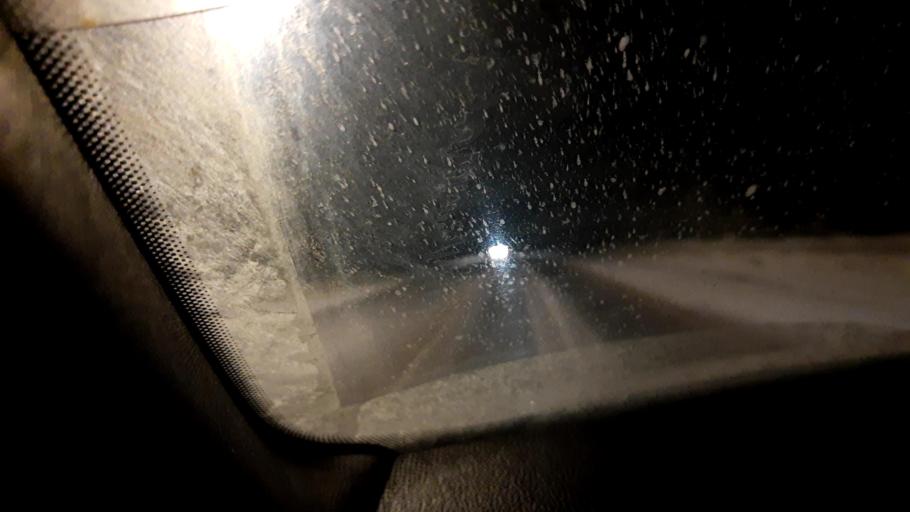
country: RU
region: Moskovskaya
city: Bogorodskoye
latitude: 56.6455
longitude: 38.1637
